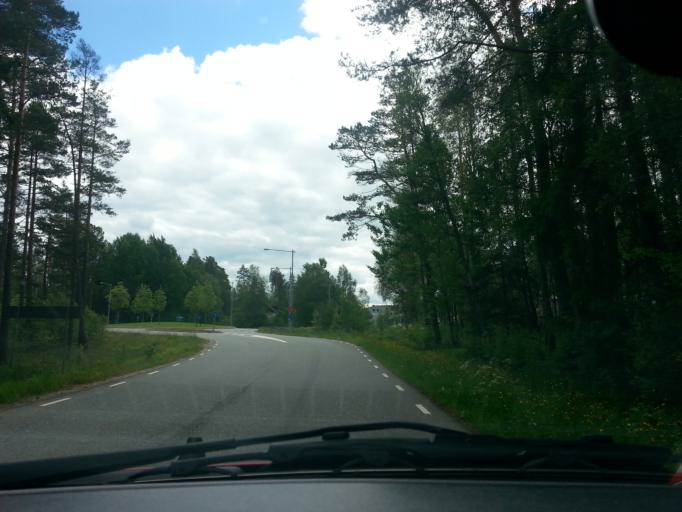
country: SE
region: Joenkoeping
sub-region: Gislaveds Kommun
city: Reftele
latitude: 57.1827
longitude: 13.5916
